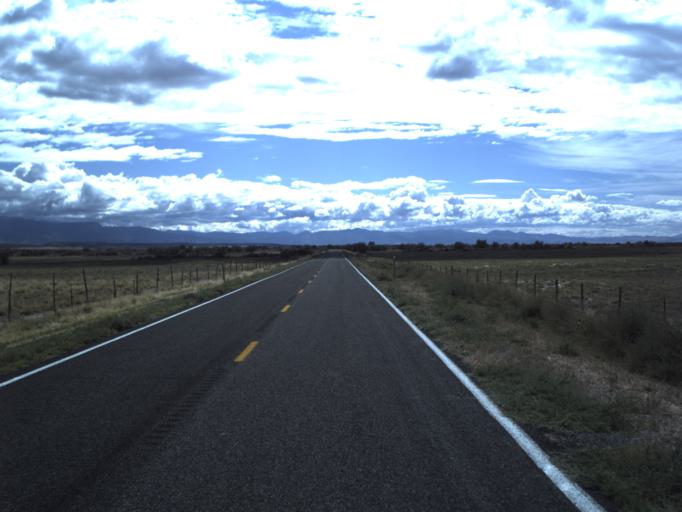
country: US
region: Utah
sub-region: Millard County
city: Fillmore
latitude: 39.1102
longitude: -112.4097
